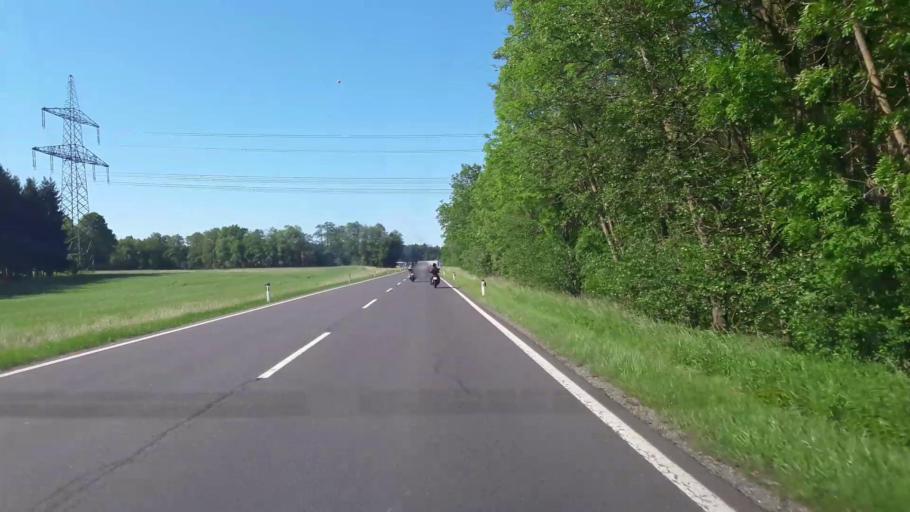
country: AT
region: Burgenland
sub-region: Politischer Bezirk Oberwart
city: Kemeten
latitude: 47.2657
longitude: 16.1521
